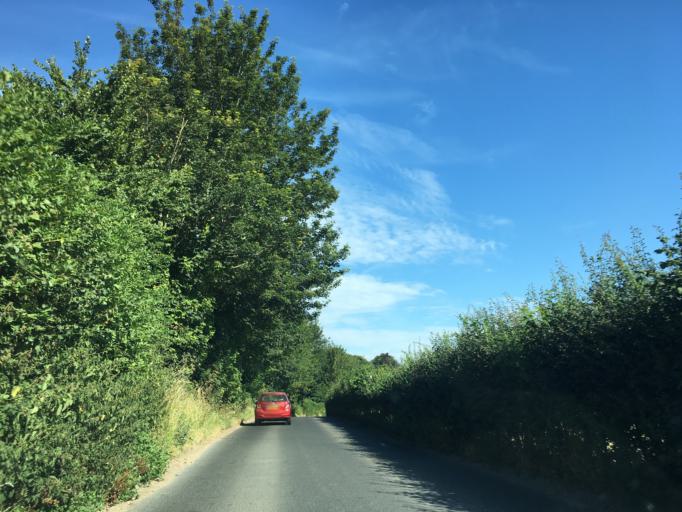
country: GB
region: England
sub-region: Isle of Wight
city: Newport
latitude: 50.6802
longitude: -1.3089
